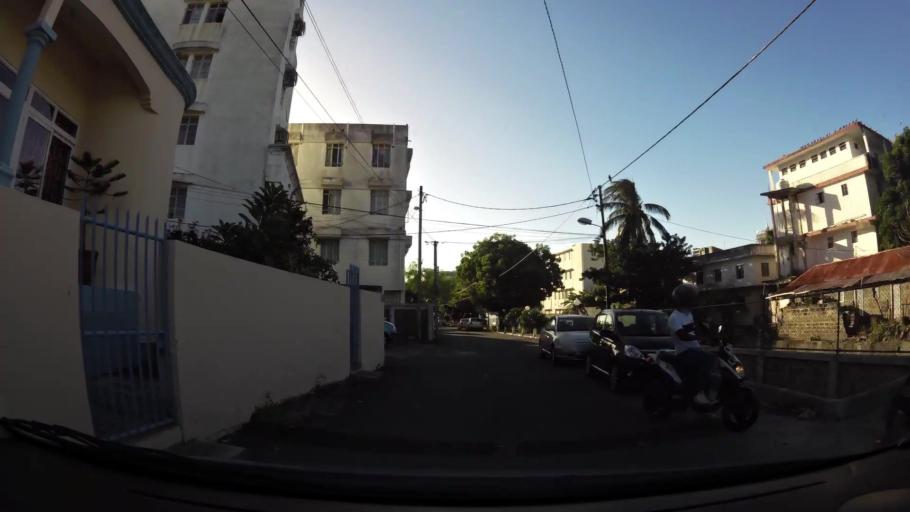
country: MU
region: Port Louis
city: Port Louis
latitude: -20.1700
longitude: 57.5058
